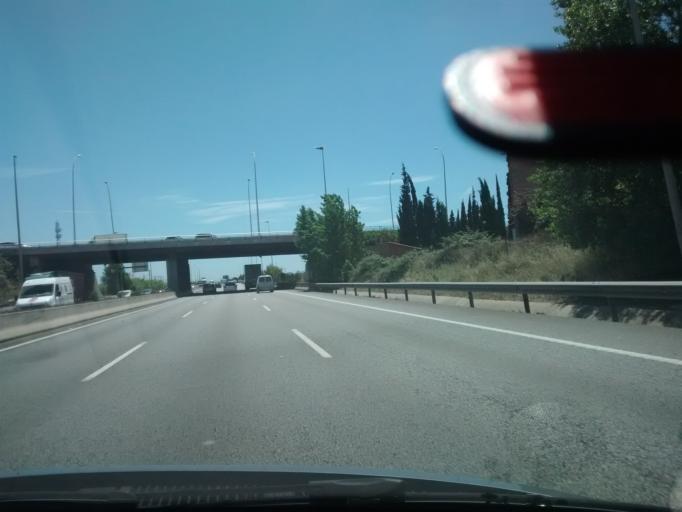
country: ES
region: Catalonia
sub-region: Provincia de Barcelona
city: Molins de Rei
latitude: 41.4085
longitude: 2.0095
